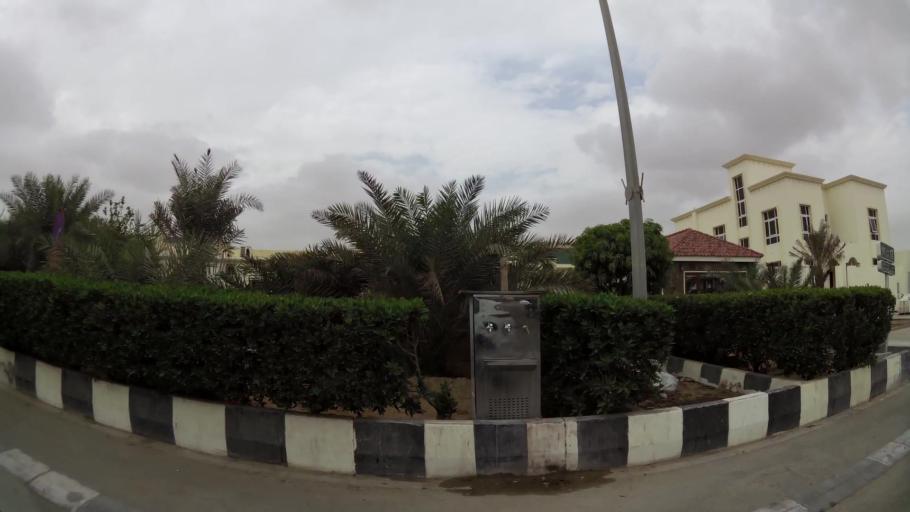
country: AE
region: Abu Dhabi
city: Abu Dhabi
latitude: 24.3479
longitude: 54.6464
